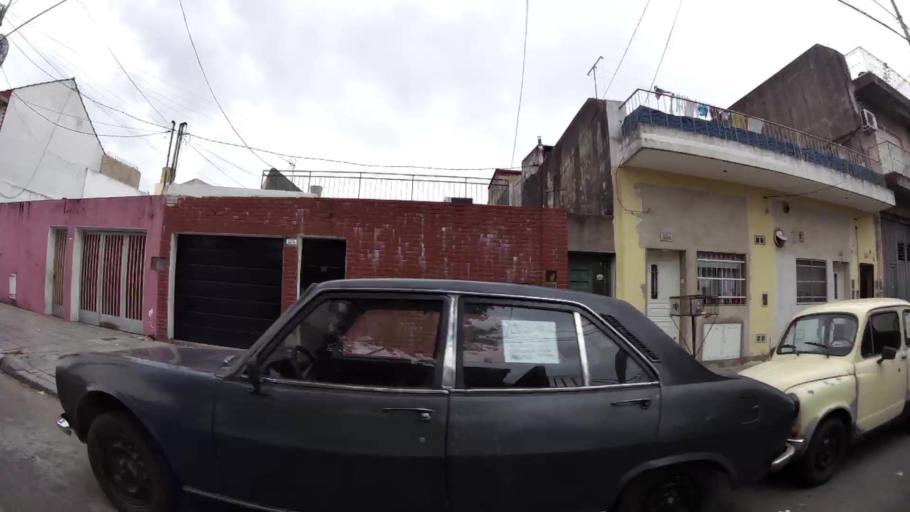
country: AR
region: Buenos Aires
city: San Justo
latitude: -34.6707
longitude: -58.5241
